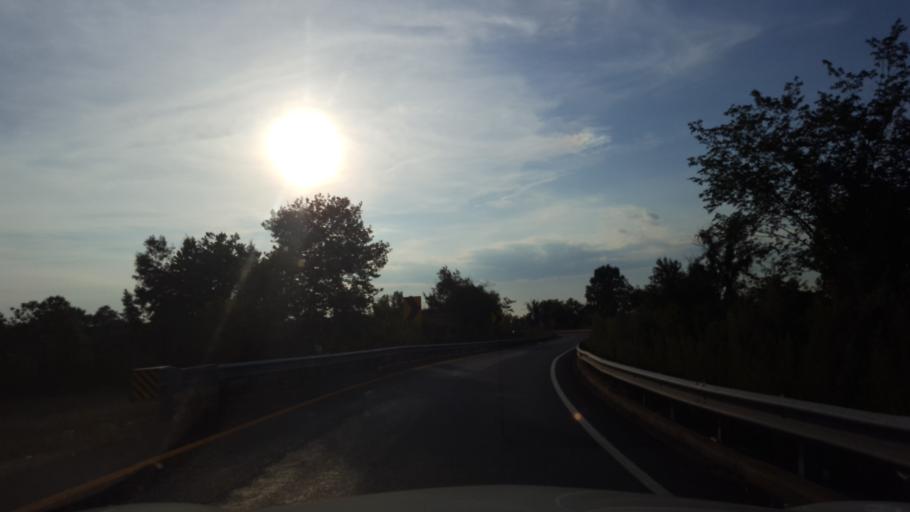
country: US
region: Delaware
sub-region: New Castle County
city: Newport
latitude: 39.7059
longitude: -75.6015
